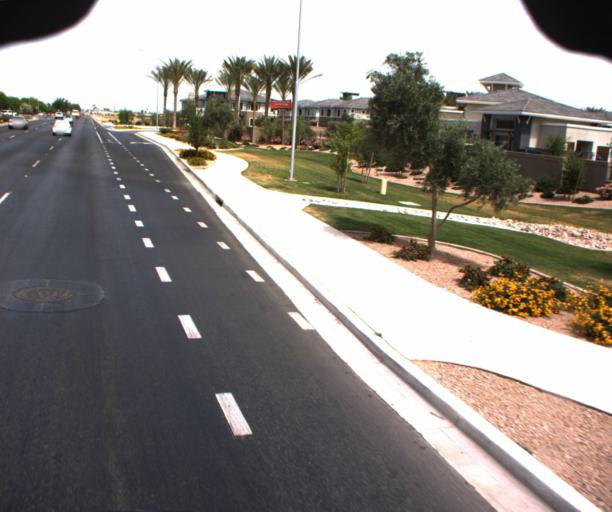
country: US
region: Arizona
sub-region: Maricopa County
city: Chandler
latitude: 33.2641
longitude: -111.8412
